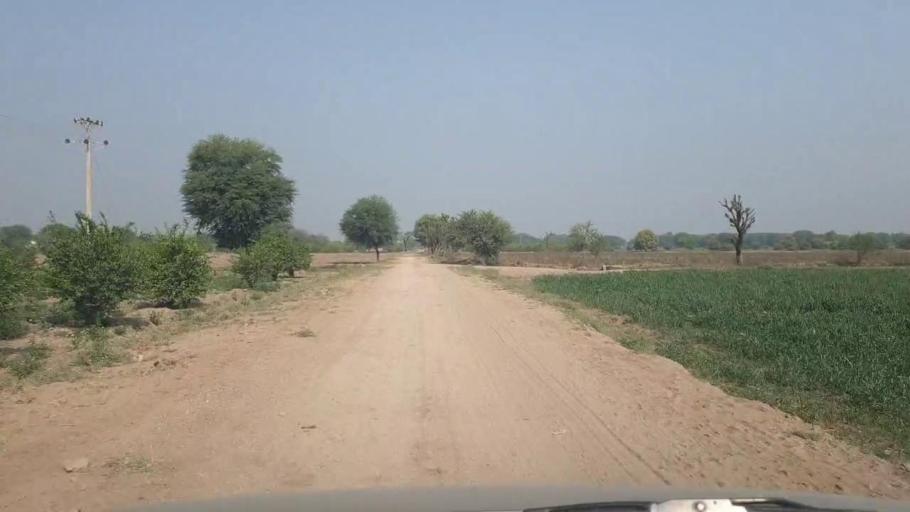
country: PK
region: Sindh
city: Umarkot
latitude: 25.3909
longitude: 69.7107
